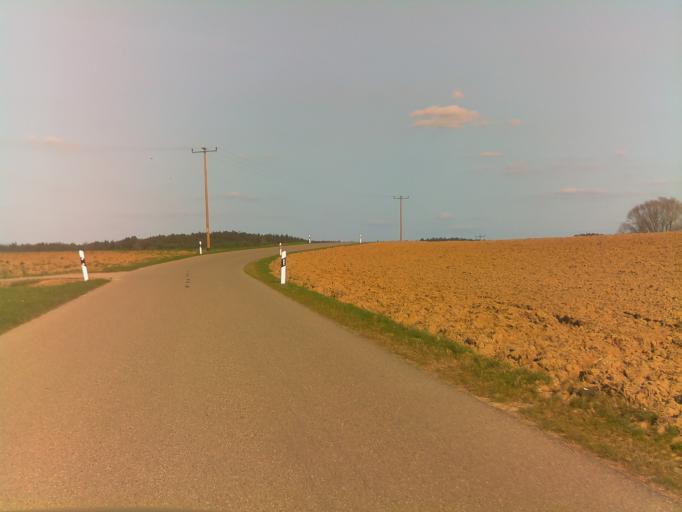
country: DE
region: Bavaria
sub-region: Upper Bavaria
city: Ehekirchen
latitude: 48.6588
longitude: 11.0641
